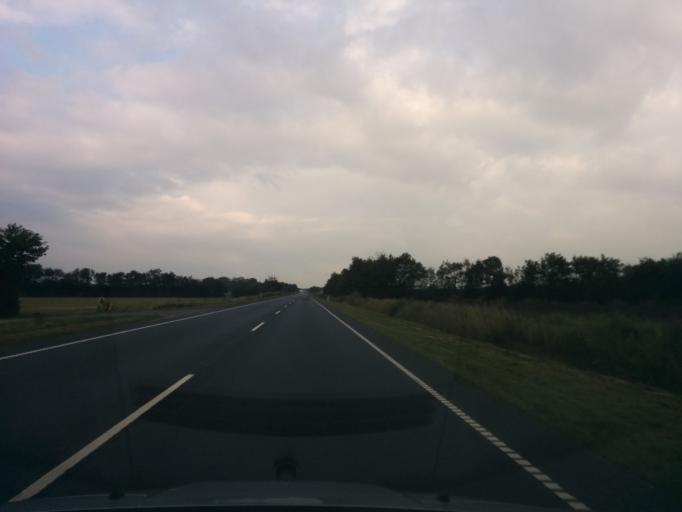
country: DK
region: South Denmark
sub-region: Esbjerg Kommune
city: Bramming
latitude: 55.6101
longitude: 8.7435
